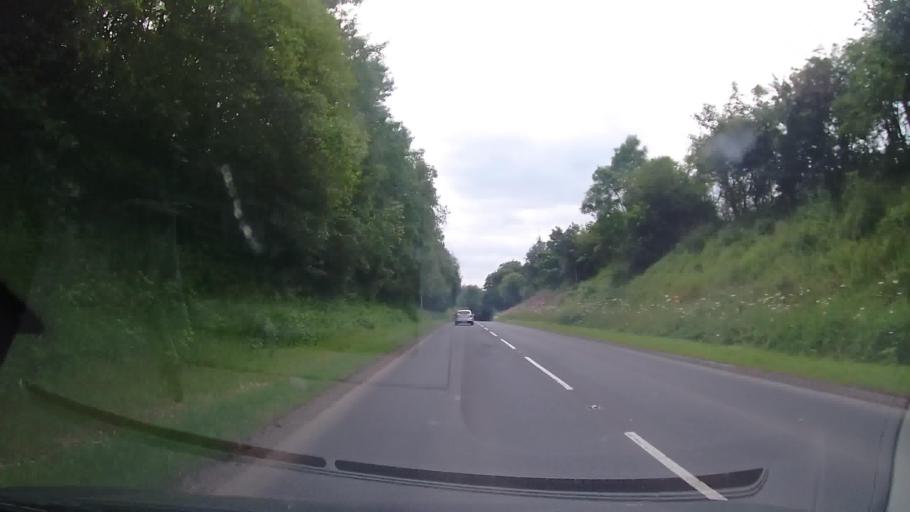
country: GB
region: Wales
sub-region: Gwynedd
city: Bala
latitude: 52.9211
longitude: -3.5639
